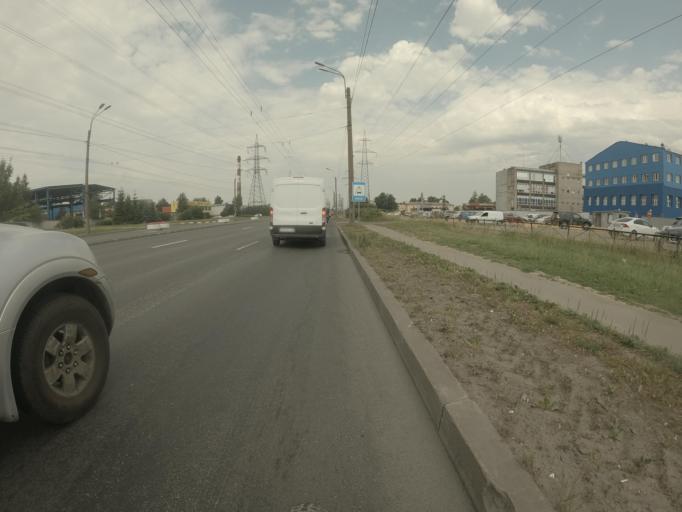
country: RU
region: St.-Petersburg
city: Krasnogvargeisky
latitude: 59.9601
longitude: 30.4627
